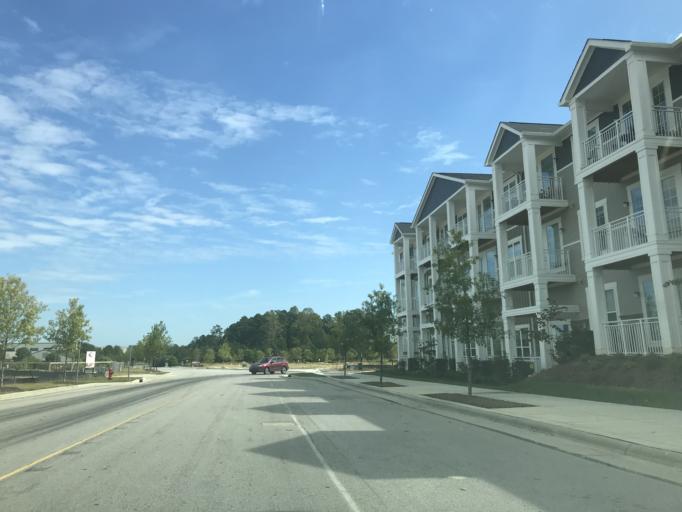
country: US
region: North Carolina
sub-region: Wake County
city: Knightdale
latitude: 35.8636
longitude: -78.5407
